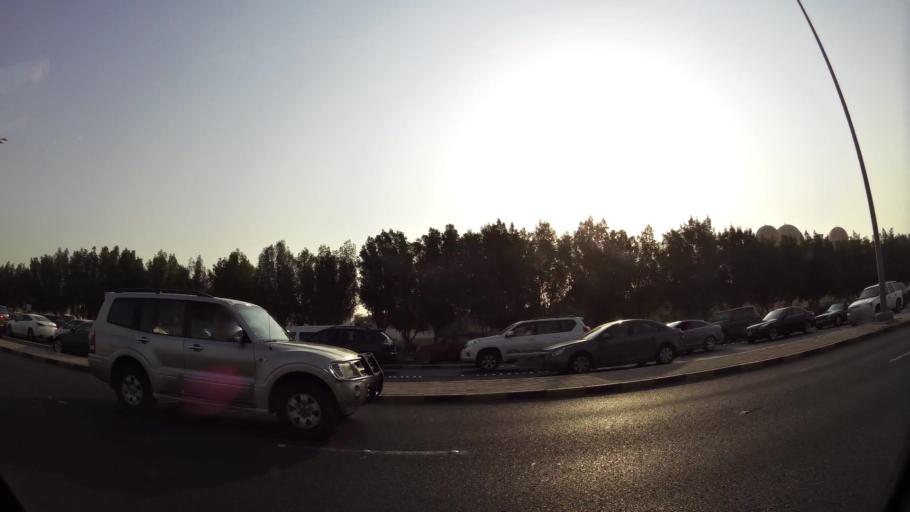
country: KW
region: Muhafazat Hawalli
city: Ar Rumaythiyah
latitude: 29.3076
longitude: 48.0858
